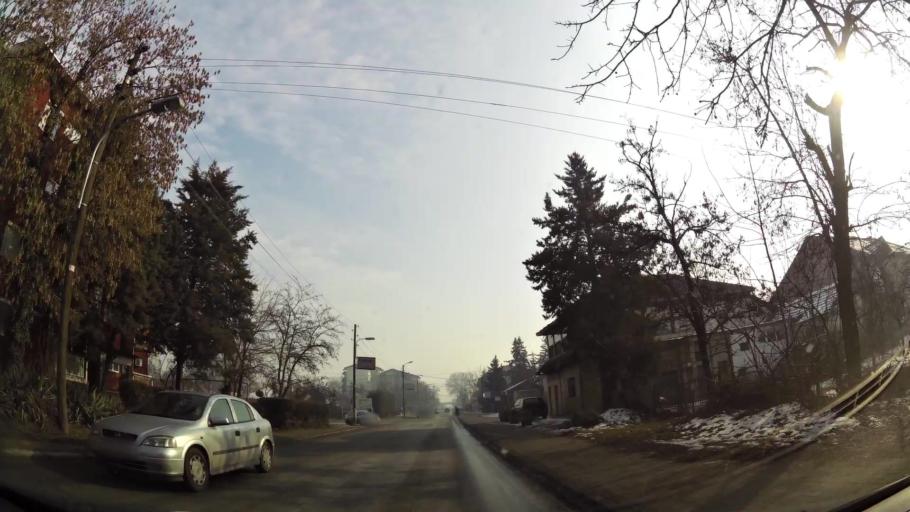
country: MK
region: Kisela Voda
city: Kisela Voda
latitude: 41.9930
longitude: 21.5069
